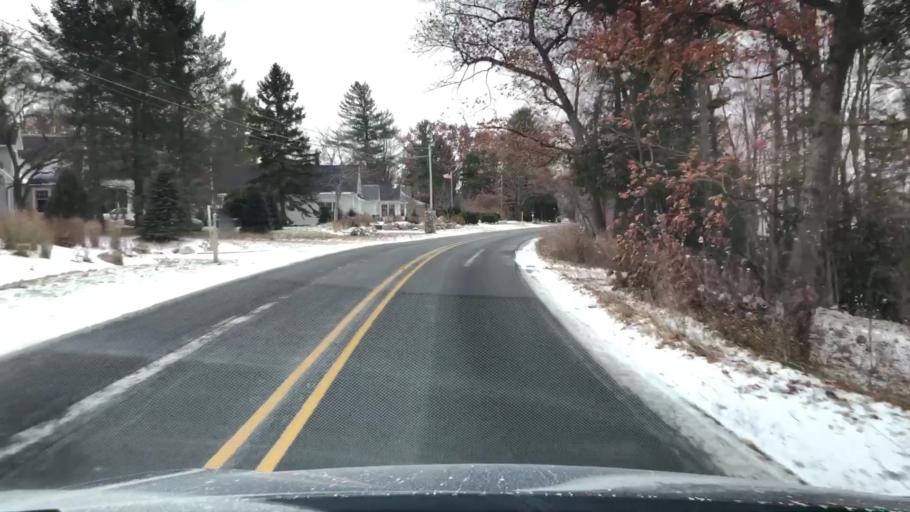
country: US
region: Michigan
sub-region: Grand Traverse County
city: Traverse City
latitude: 44.8128
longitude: -85.5787
